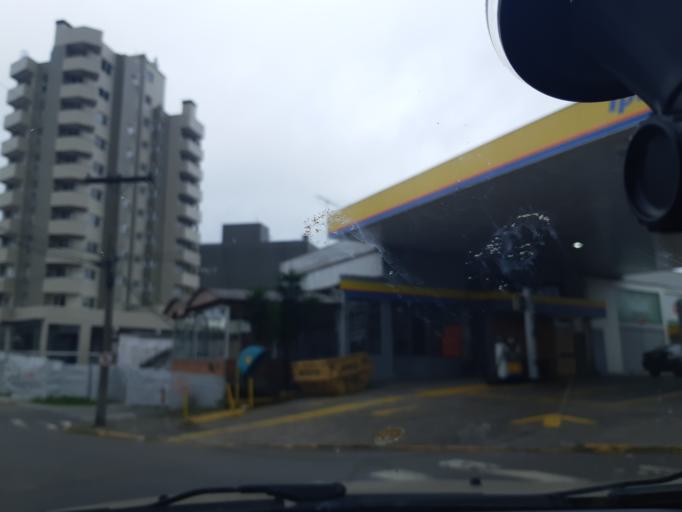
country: BR
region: Rio Grande do Sul
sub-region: Caxias Do Sul
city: Caxias do Sul
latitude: -29.1582
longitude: -51.1973
